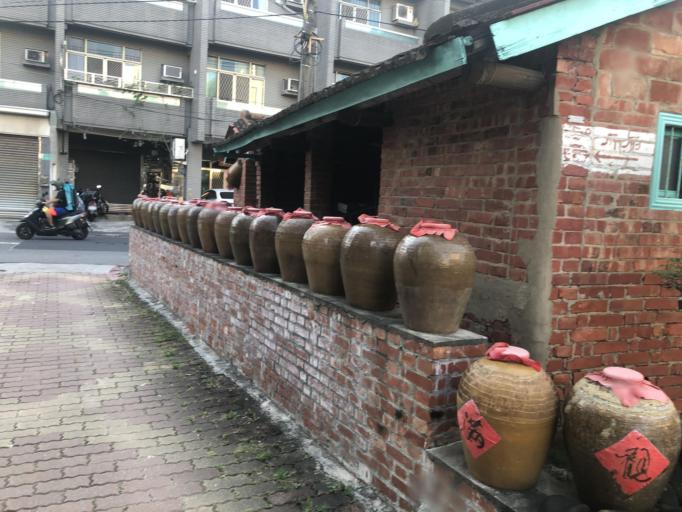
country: TW
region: Taiwan
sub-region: Tainan
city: Tainan
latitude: 23.0412
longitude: 120.1843
